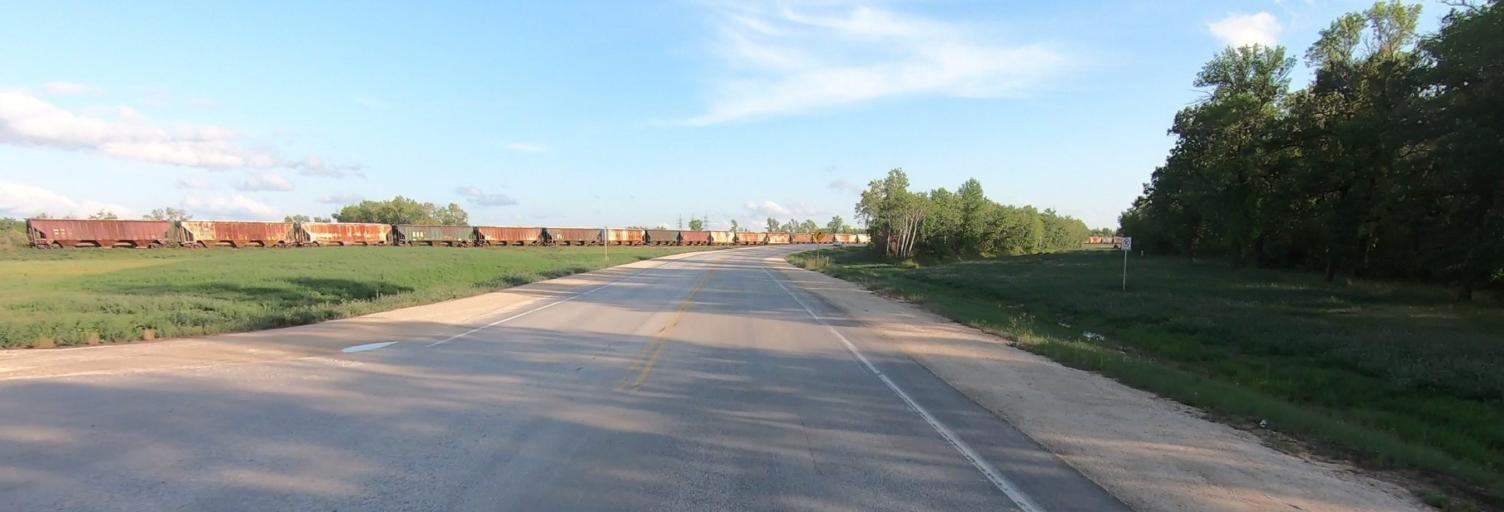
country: CA
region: Manitoba
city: Selkirk
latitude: 50.1327
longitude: -96.8533
